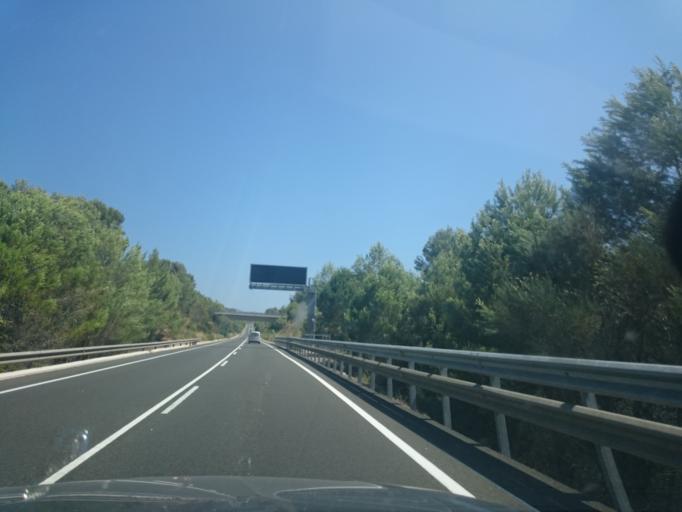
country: ES
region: Catalonia
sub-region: Provincia de Barcelona
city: Sant Pere de Riudebitlles
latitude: 41.4859
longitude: 1.7026
